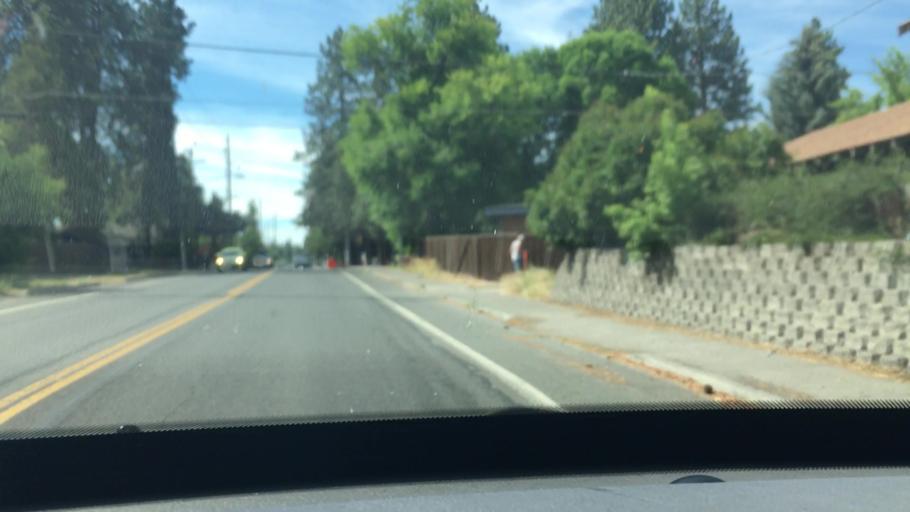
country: US
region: Oregon
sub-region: Deschutes County
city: Bend
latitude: 44.0542
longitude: -121.3319
